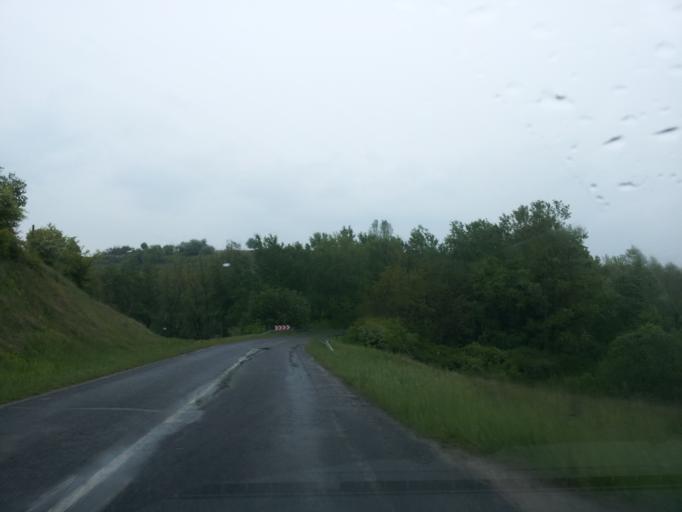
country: HU
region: Tolna
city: Bonyhad
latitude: 46.2685
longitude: 18.6217
